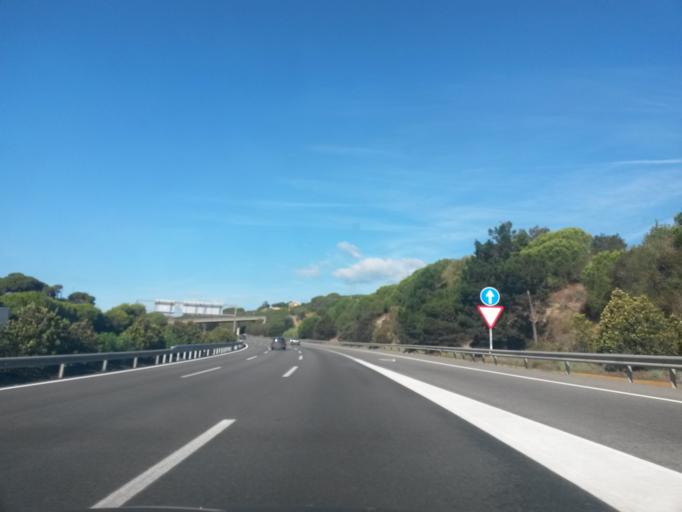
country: ES
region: Catalonia
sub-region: Provincia de Barcelona
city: Canet de Mar
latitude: 41.5950
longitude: 2.5656
